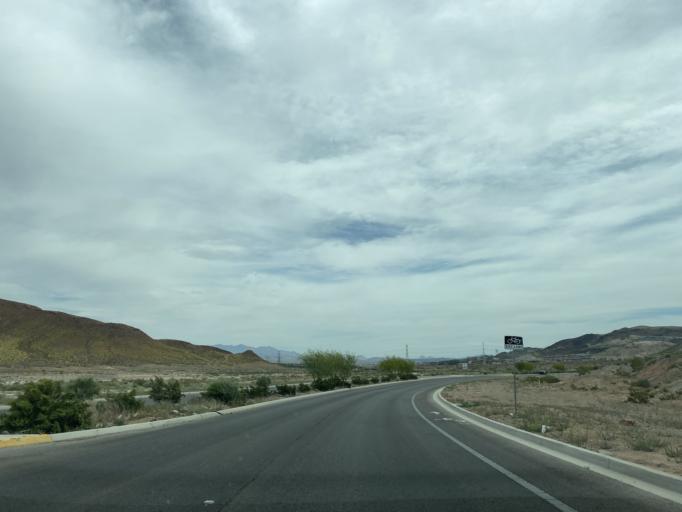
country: US
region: Nevada
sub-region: Clark County
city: Henderson
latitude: 36.0931
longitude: -114.9551
